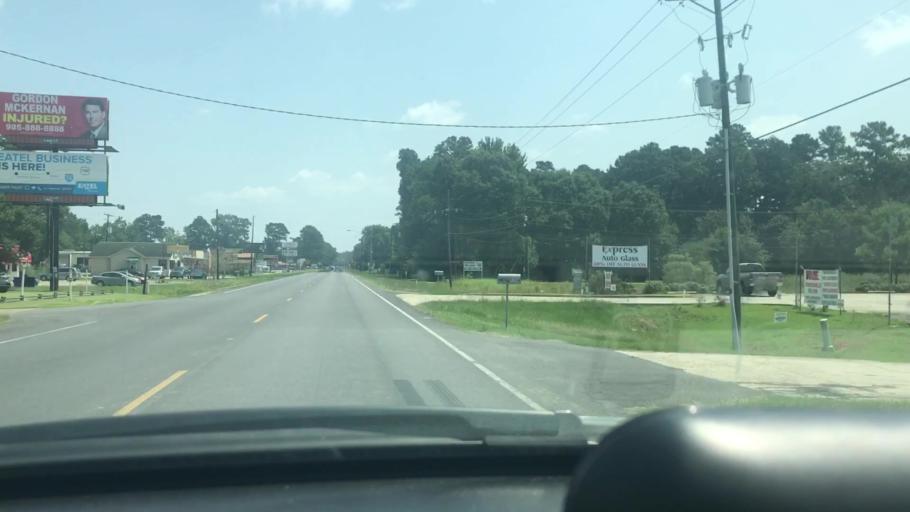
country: US
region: Louisiana
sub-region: Livingston Parish
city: Walker
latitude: 30.4870
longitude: -90.8734
